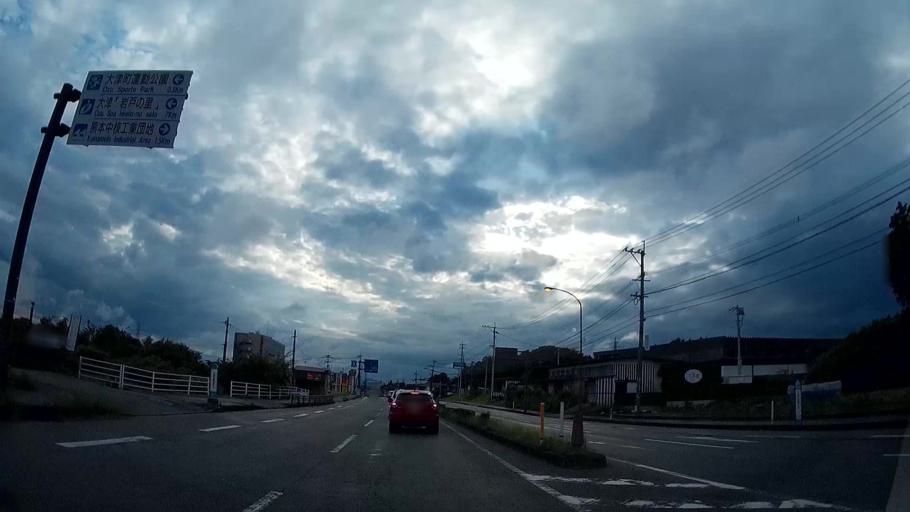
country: JP
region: Kumamoto
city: Ozu
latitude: 32.8804
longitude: 130.8958
